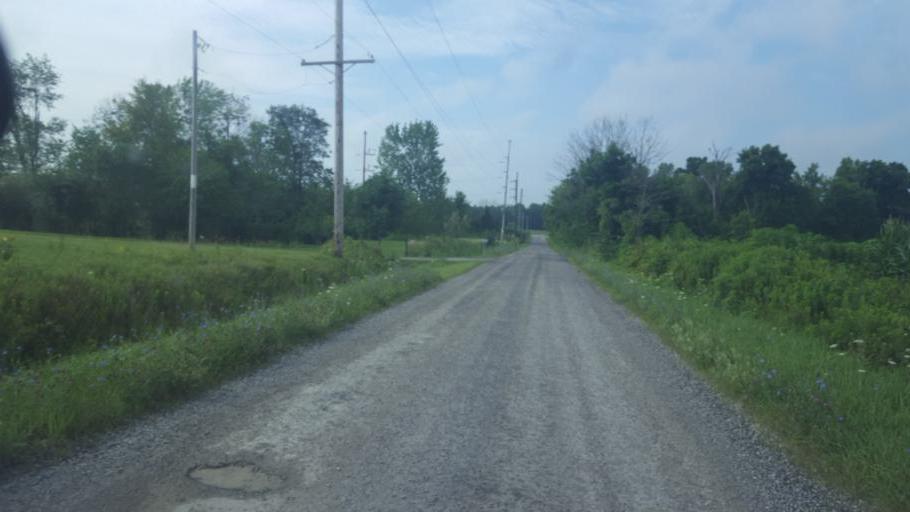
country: US
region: Ohio
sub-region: Delaware County
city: Ashley
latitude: 40.3696
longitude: -82.9115
